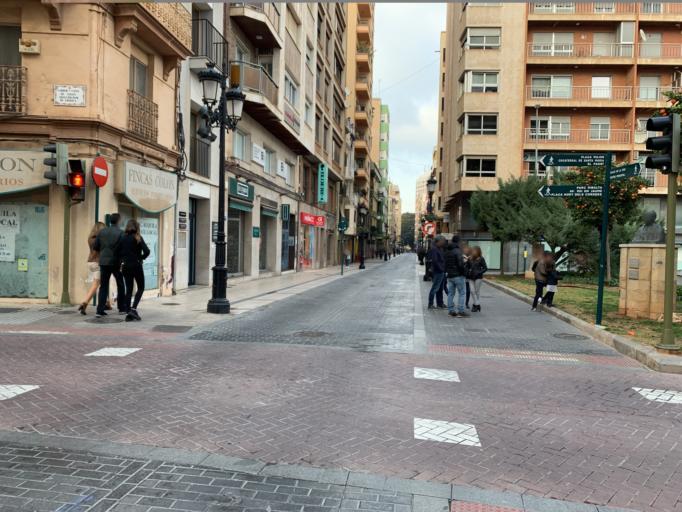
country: ES
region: Valencia
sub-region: Provincia de Castello
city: Castello de la Plana
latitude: 39.9862
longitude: -0.0362
